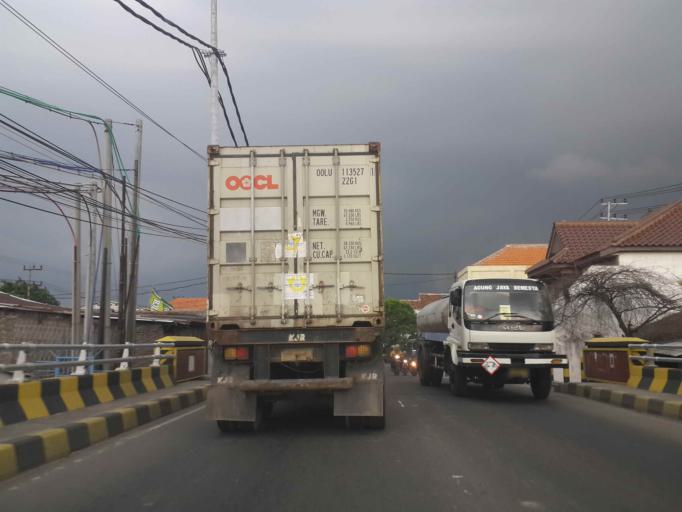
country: ID
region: East Java
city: Kebomas
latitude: -7.2101
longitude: 112.6522
